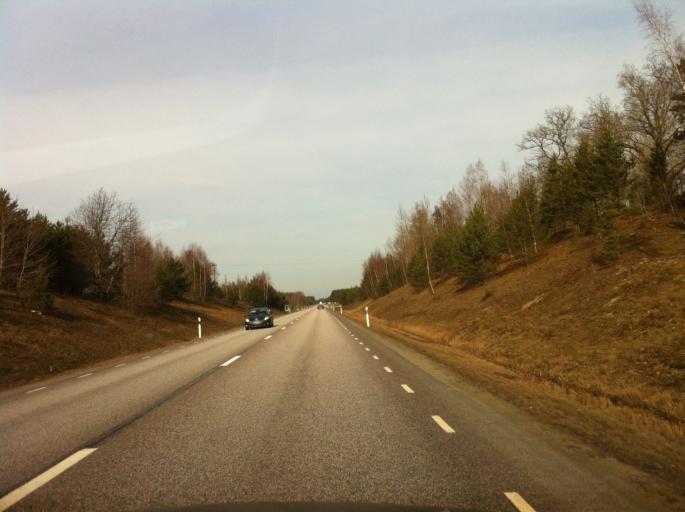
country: SE
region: Vaestra Goetaland
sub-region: Mariestads Kommun
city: Mariestad
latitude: 58.8020
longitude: 13.9730
